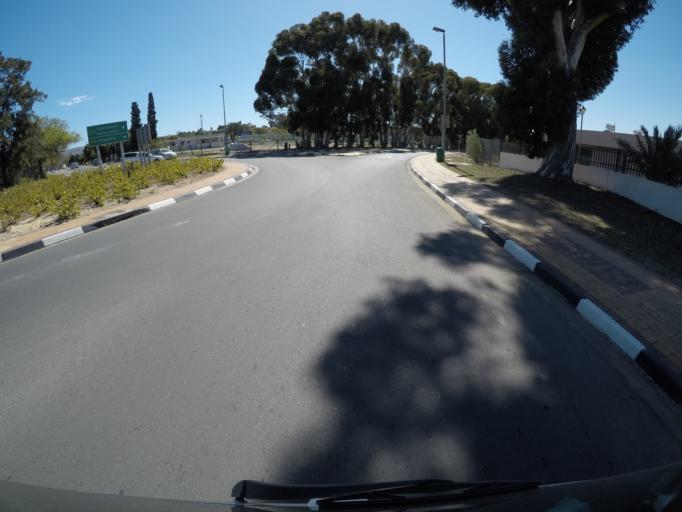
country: ZA
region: Western Cape
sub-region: City of Cape Town
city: Kraaifontein
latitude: -33.8304
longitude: 18.6447
